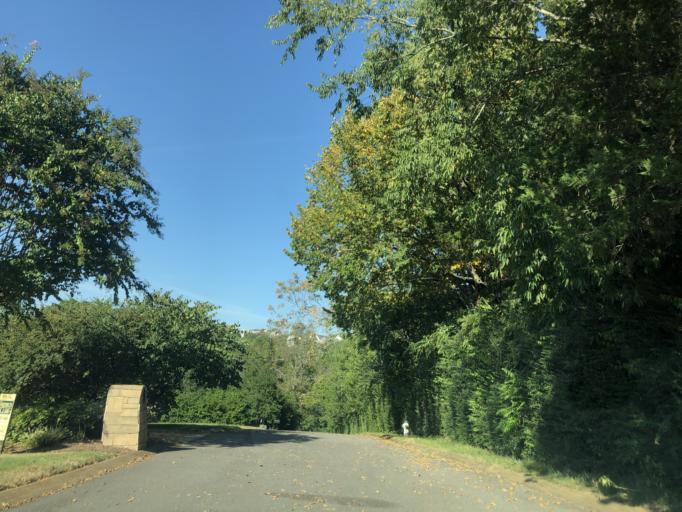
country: US
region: Tennessee
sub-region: Davidson County
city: Forest Hills
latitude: 36.0900
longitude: -86.8326
